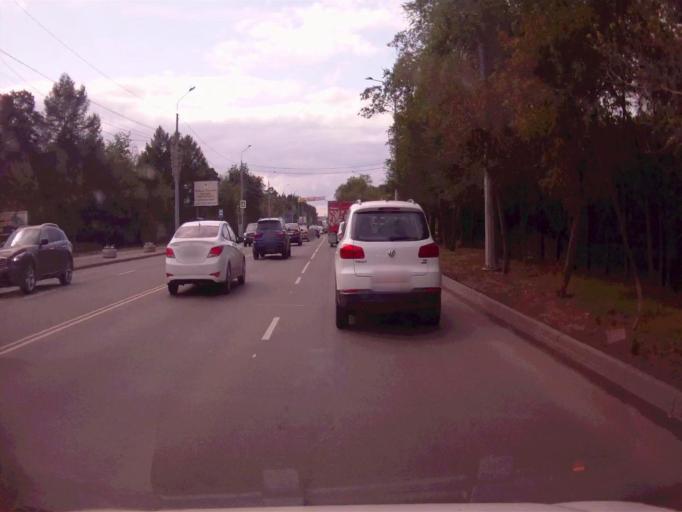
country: RU
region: Chelyabinsk
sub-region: Gorod Chelyabinsk
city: Chelyabinsk
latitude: 55.1473
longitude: 61.3599
